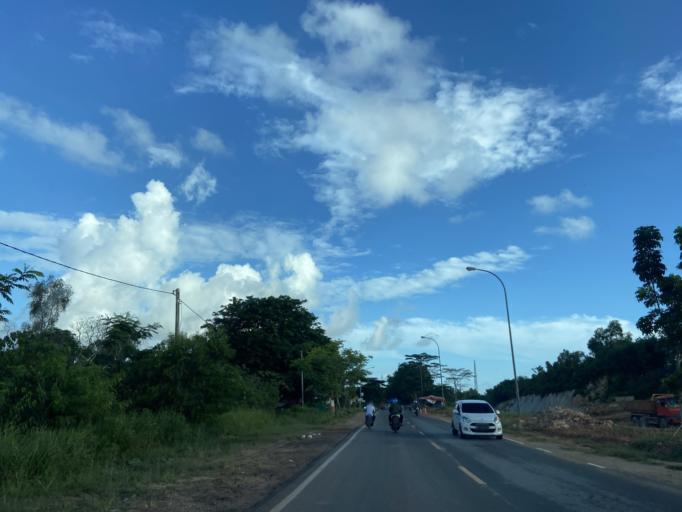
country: SG
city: Singapore
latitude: 1.0234
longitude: 104.0110
